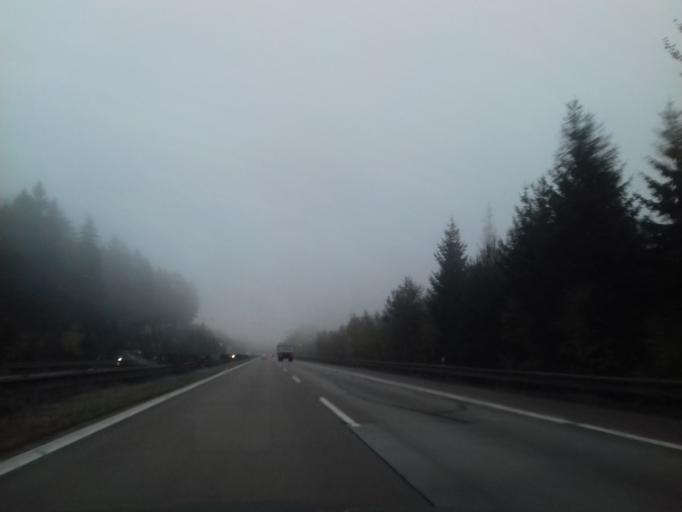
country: CZ
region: Vysocina
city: Heralec
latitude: 49.4904
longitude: 15.5028
